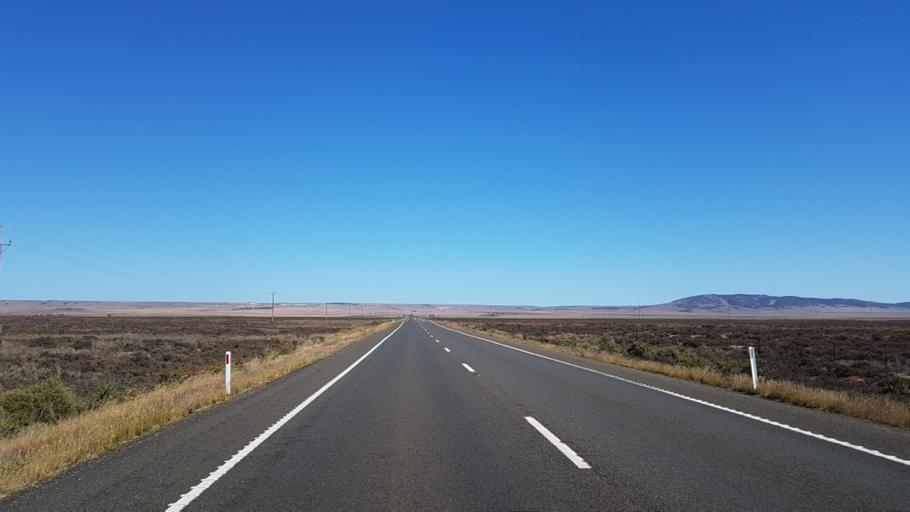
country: AU
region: South Australia
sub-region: Wakefield
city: Balaklava
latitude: -34.1122
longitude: 138.1218
